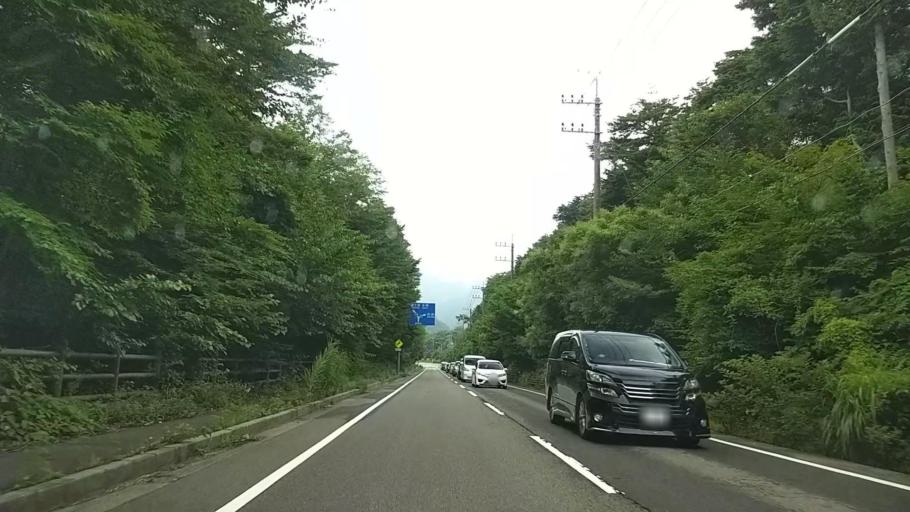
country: JP
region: Yamanashi
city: Fujikawaguchiko
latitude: 35.4861
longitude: 138.6477
